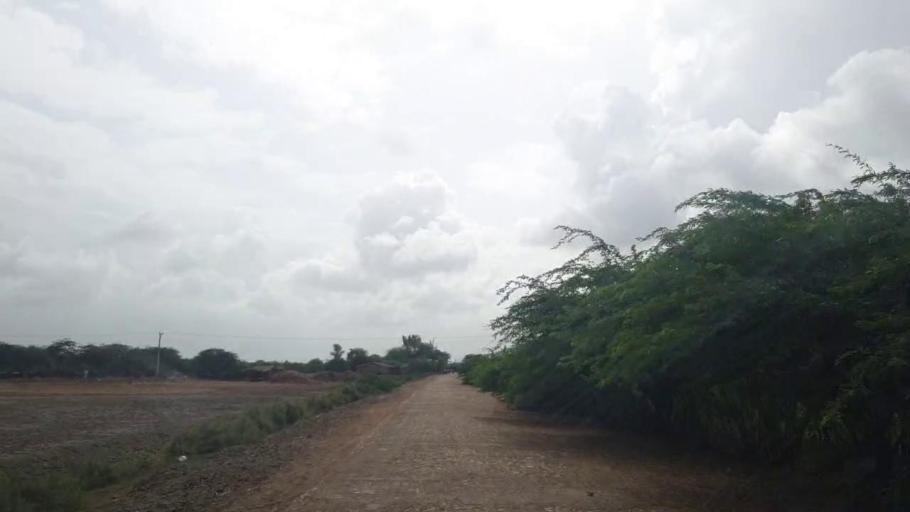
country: PK
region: Sindh
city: Tando Bago
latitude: 24.8265
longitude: 69.0770
